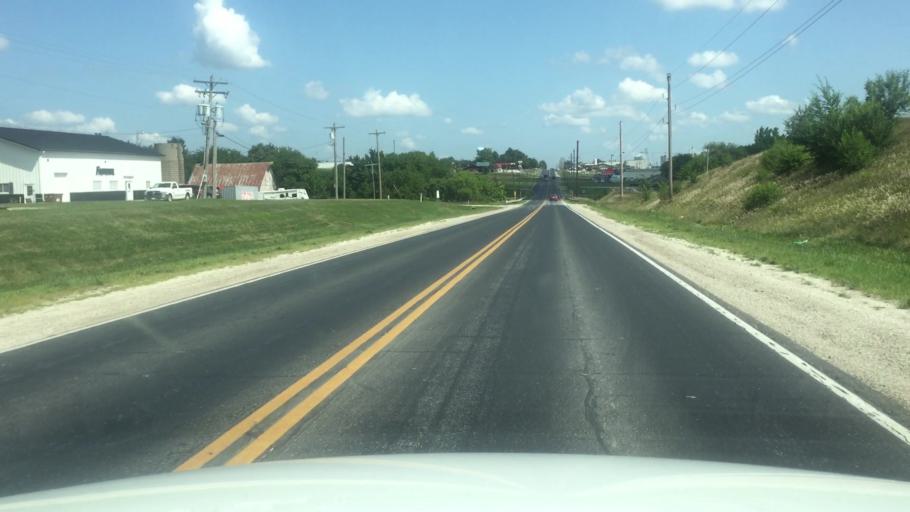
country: US
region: Kansas
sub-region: Nemaha County
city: Sabetha
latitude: 39.8870
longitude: -95.7883
